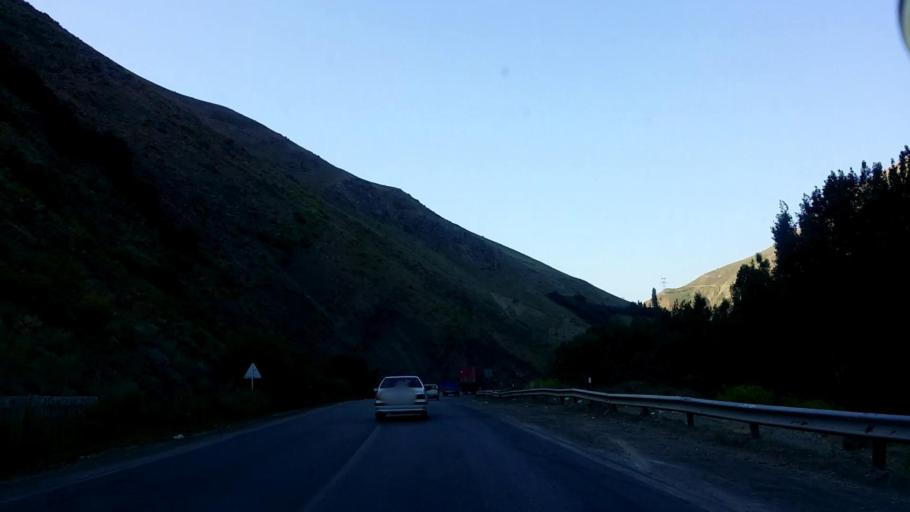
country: IR
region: Tehran
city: Tajrish
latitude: 36.1098
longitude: 51.3192
